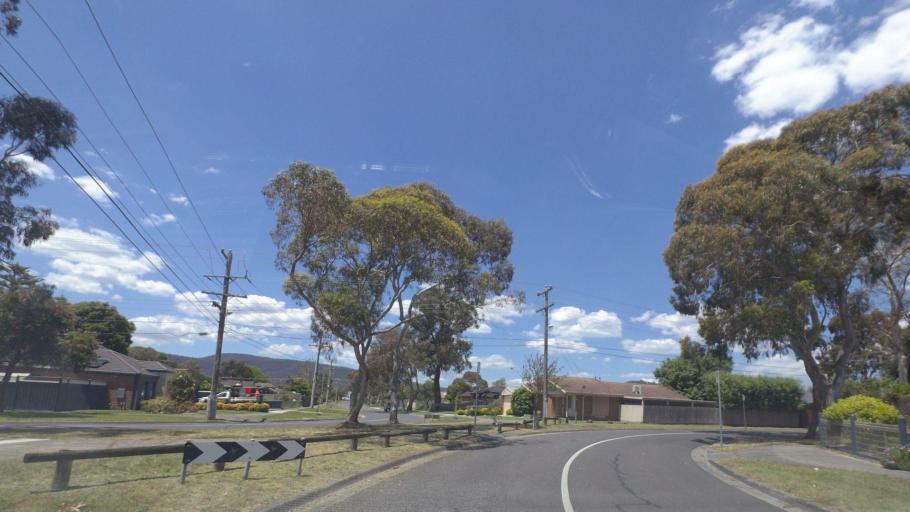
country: AU
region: Victoria
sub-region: Knox
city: Knoxfield
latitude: -37.8839
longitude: 145.2652
